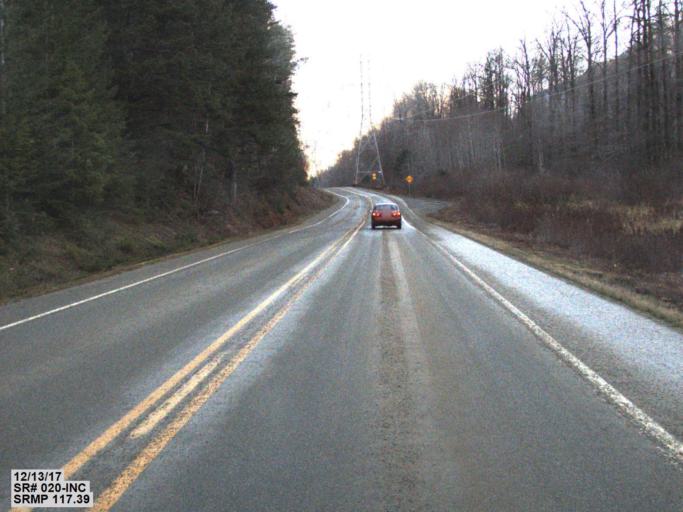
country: US
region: Washington
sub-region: Snohomish County
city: Darrington
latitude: 48.6514
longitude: -121.3012
